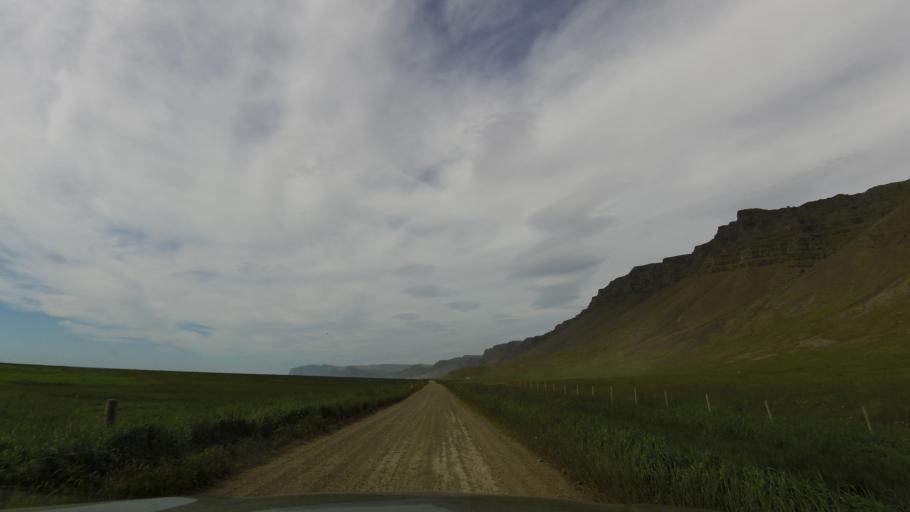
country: IS
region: West
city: Olafsvik
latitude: 65.4788
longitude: -24.0065
